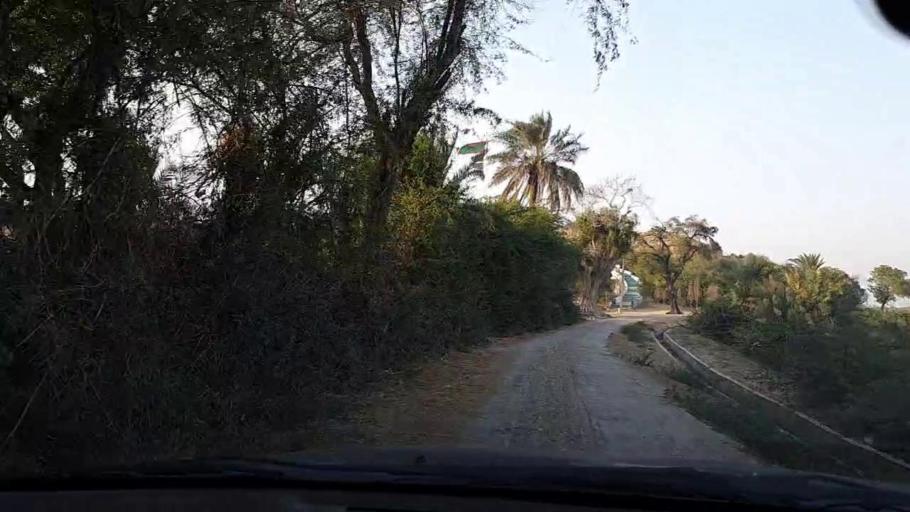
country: PK
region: Sindh
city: Thatta
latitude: 24.5605
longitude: 67.8802
